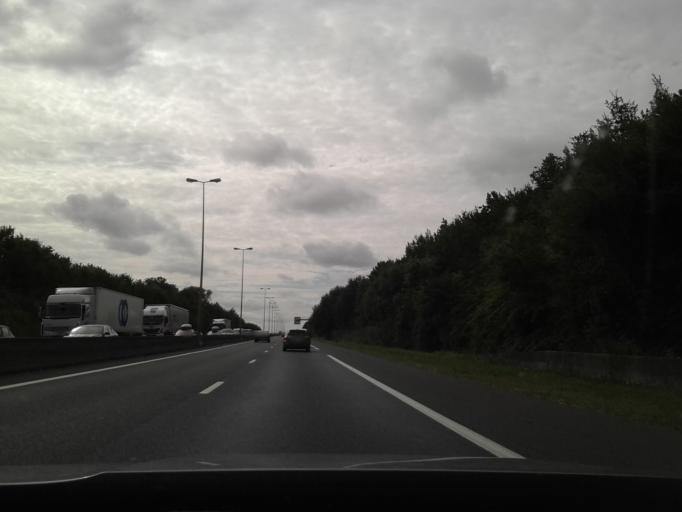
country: FR
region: Lower Normandy
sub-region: Departement du Calvados
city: Bretteville-sur-Odon
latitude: 49.1569
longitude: -0.4242
